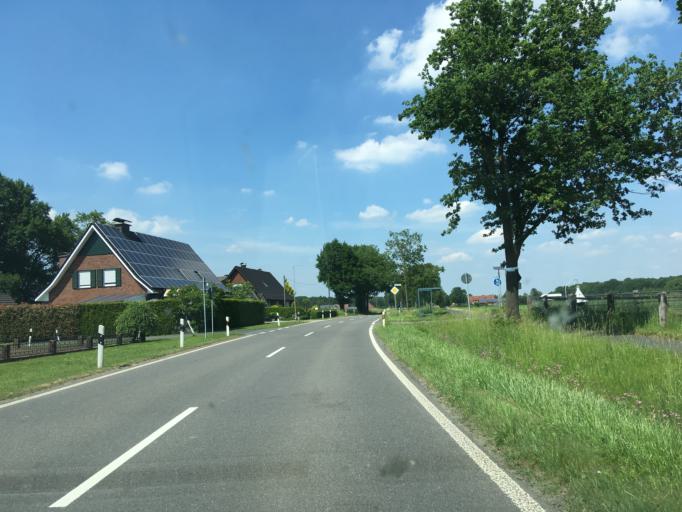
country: DE
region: North Rhine-Westphalia
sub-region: Regierungsbezirk Munster
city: Borken
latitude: 51.8450
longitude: 6.7799
